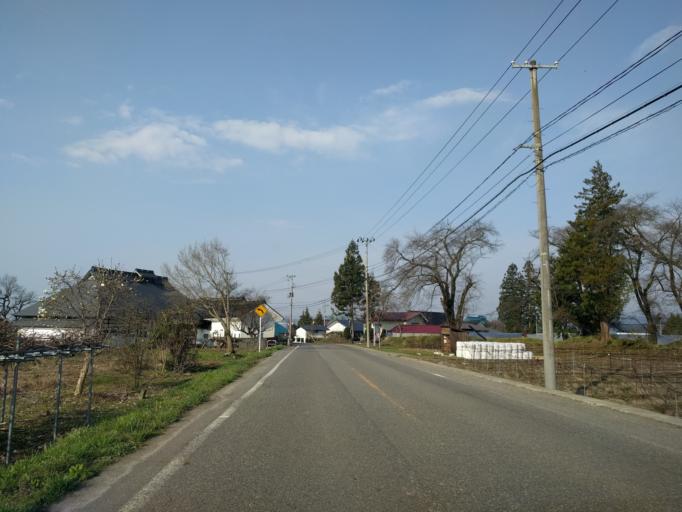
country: JP
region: Fukushima
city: Kitakata
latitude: 37.6786
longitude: 139.8965
